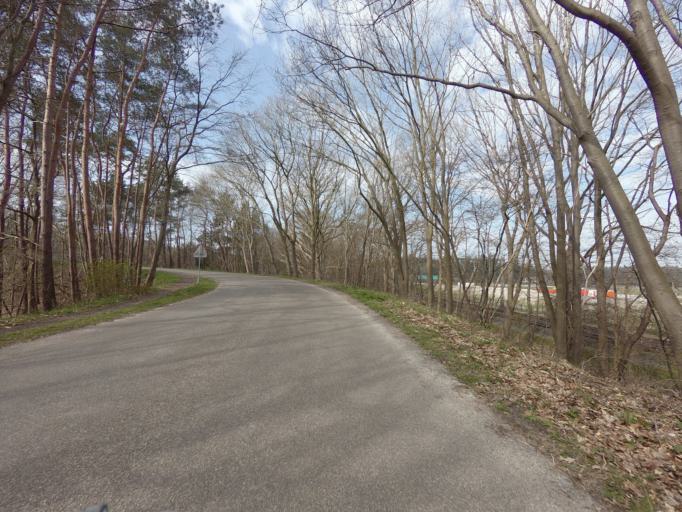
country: NL
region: Gelderland
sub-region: Gemeente Harderwijk
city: Harderwijk
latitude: 52.3438
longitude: 5.7044
